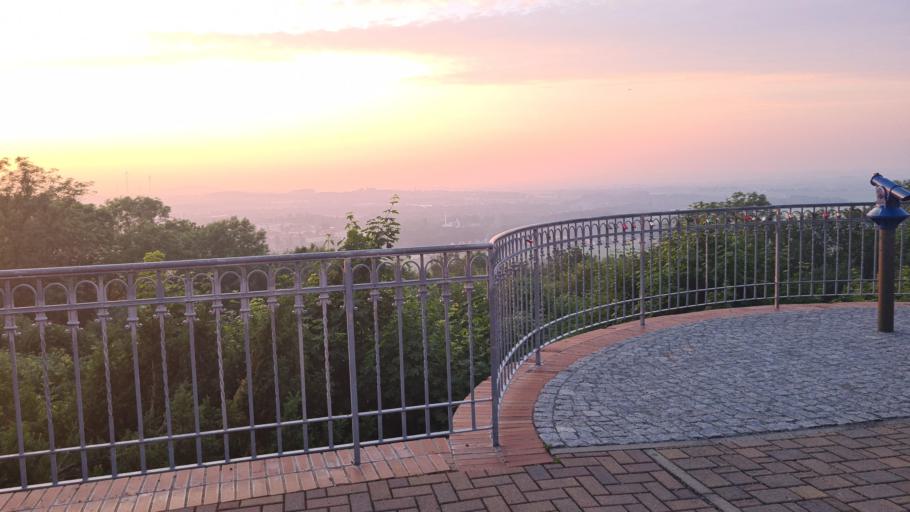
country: DE
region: Saxony
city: Lobau
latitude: 51.0955
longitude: 14.6932
